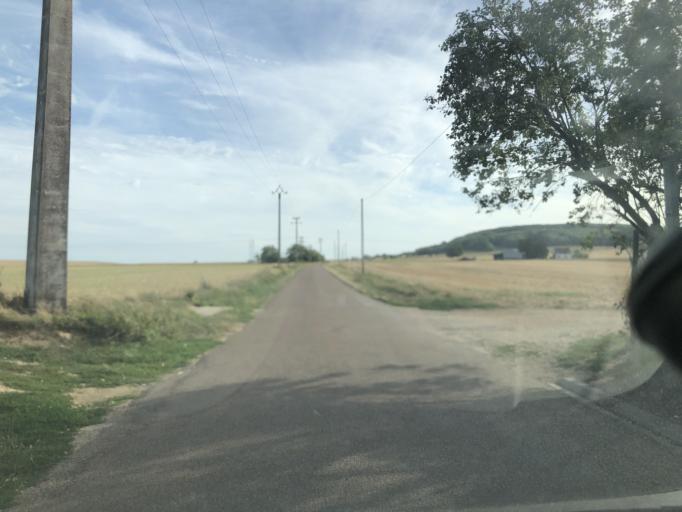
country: FR
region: Bourgogne
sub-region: Departement de l'Yonne
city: Joigny
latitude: 47.9537
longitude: 3.3991
